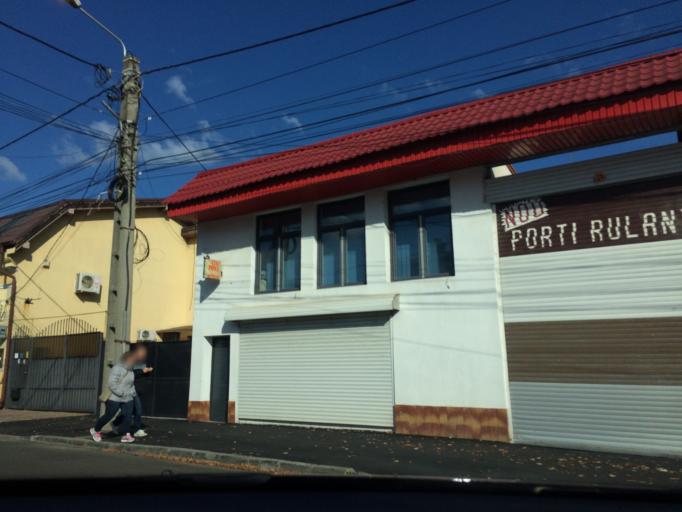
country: RO
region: Timis
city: Timisoara
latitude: 45.7617
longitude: 21.2092
